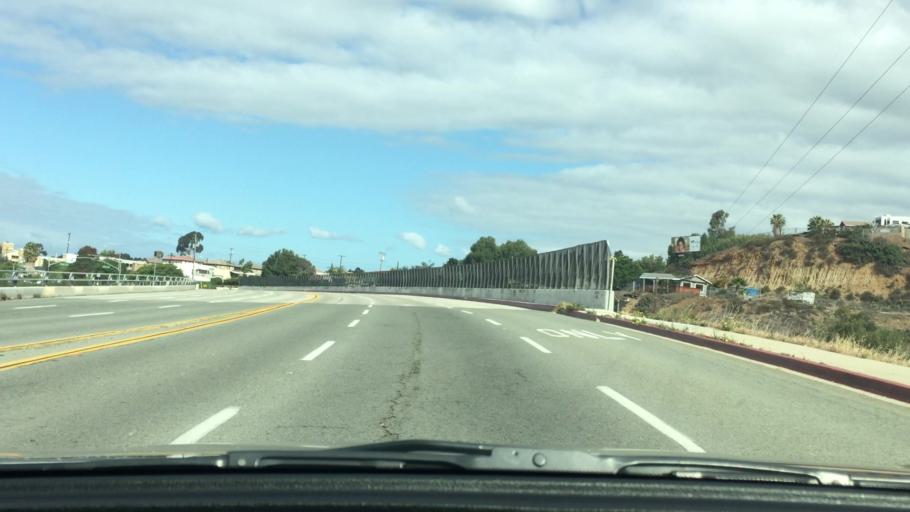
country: US
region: California
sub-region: San Diego County
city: Chula Vista
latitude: 32.6604
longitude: -117.0676
